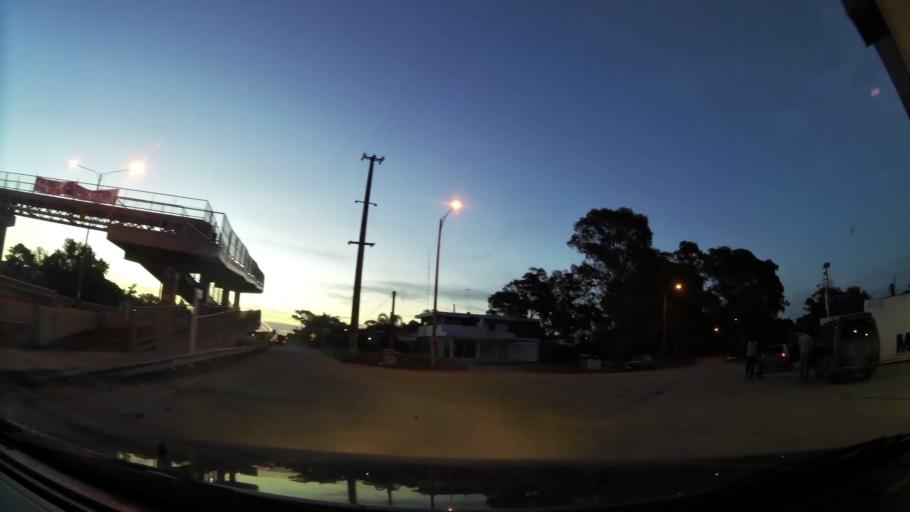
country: UY
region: Canelones
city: Atlantida
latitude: -34.7652
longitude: -55.7555
